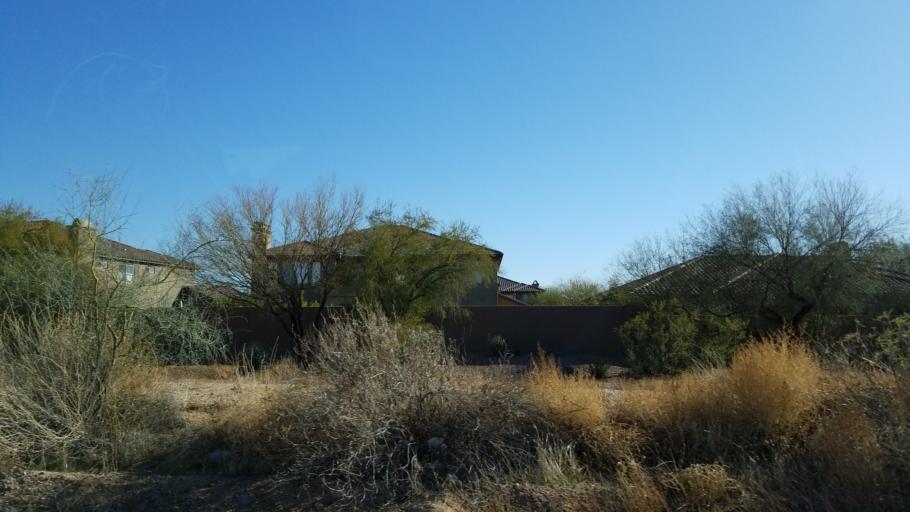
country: US
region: Arizona
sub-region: Maricopa County
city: Cave Creek
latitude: 33.6987
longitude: -111.9892
